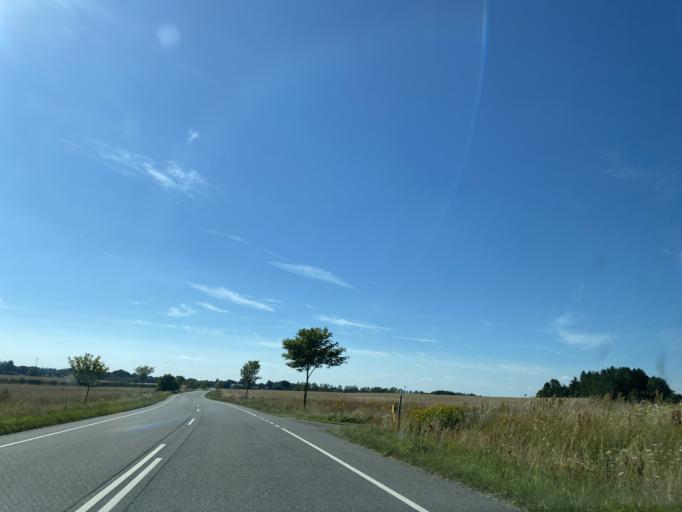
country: DK
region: Central Jutland
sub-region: Hedensted Kommune
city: Torring
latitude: 55.8670
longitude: 9.3801
